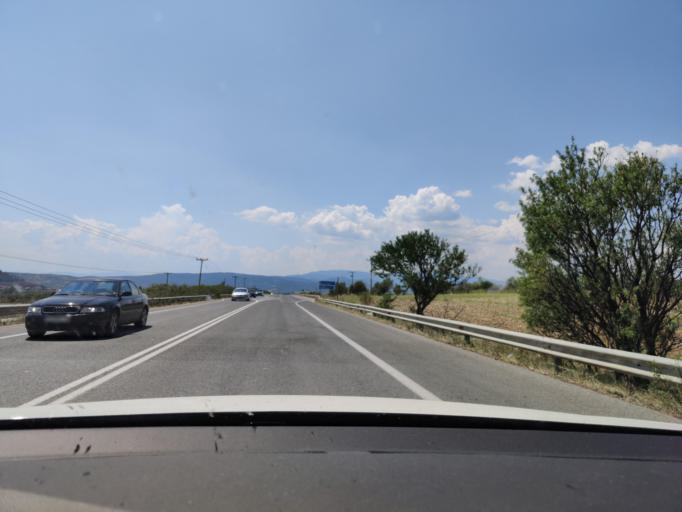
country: GR
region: Central Macedonia
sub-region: Nomos Serron
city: Palaiokomi
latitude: 40.8644
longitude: 23.8646
